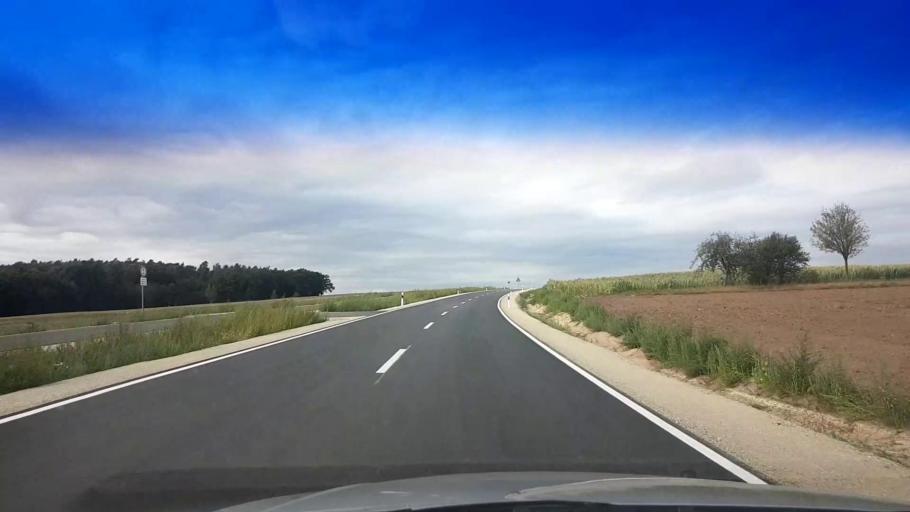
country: DE
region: Bavaria
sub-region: Upper Franconia
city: Frensdorf
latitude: 49.7980
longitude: 10.8778
